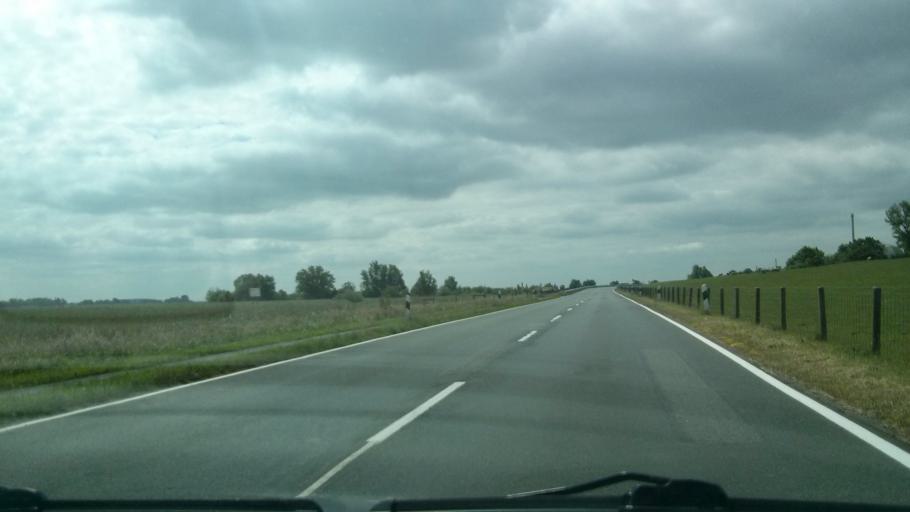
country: DE
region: Lower Saxony
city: Nordenham
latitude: 53.4402
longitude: 8.4793
